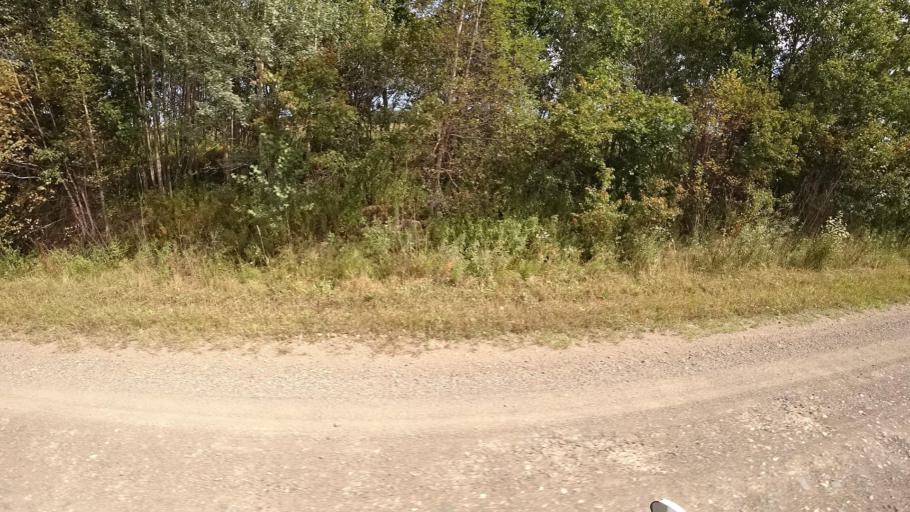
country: RU
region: Primorskiy
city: Yakovlevka
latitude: 44.7182
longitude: 133.6167
